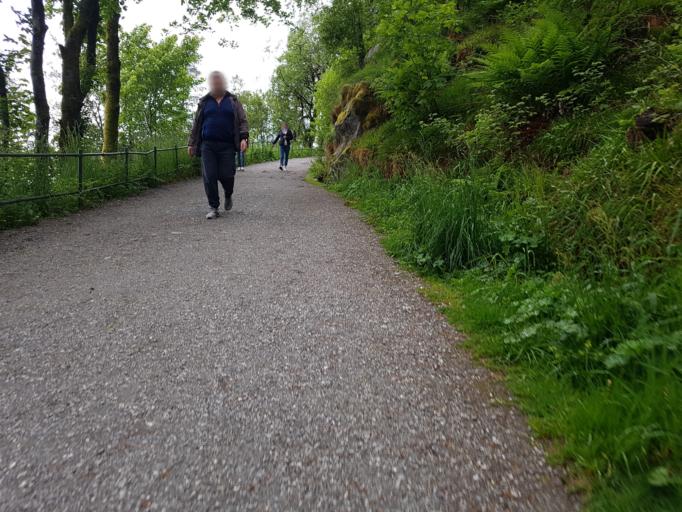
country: NO
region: Hordaland
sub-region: Bergen
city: Bergen
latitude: 60.3971
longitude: 5.3388
